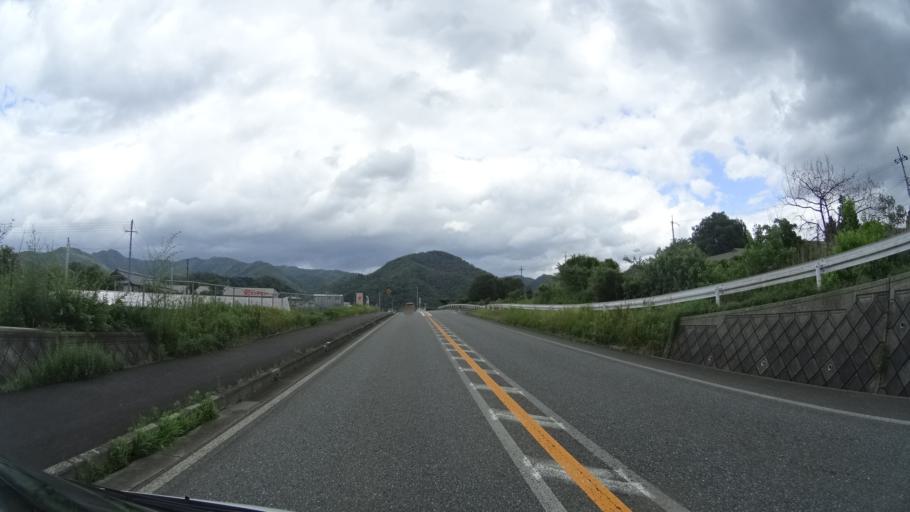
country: JP
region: Kyoto
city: Ayabe
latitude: 35.2037
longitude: 135.4321
